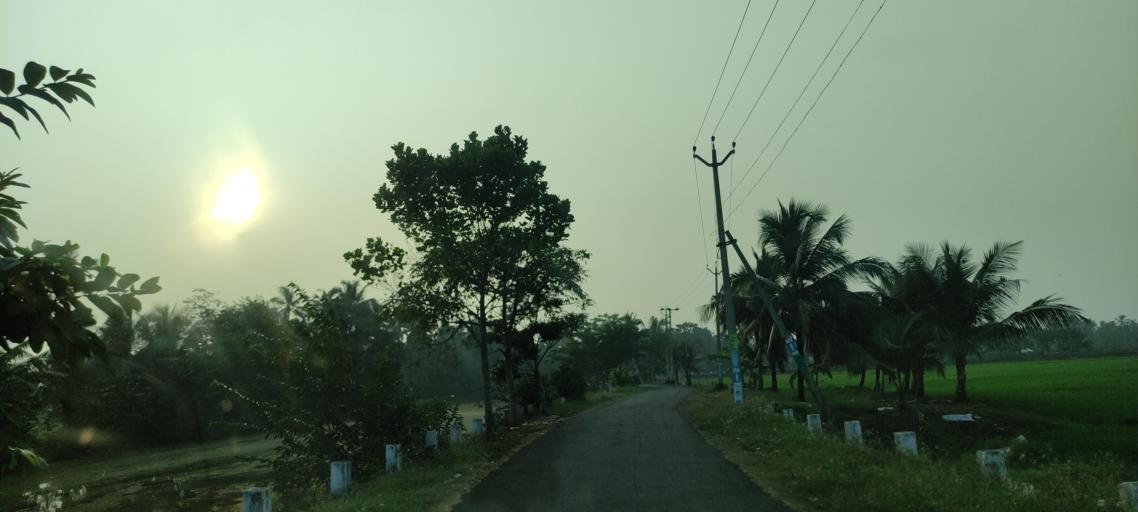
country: IN
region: Kerala
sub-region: Kottayam
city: Vaikam
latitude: 9.6839
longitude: 76.4641
